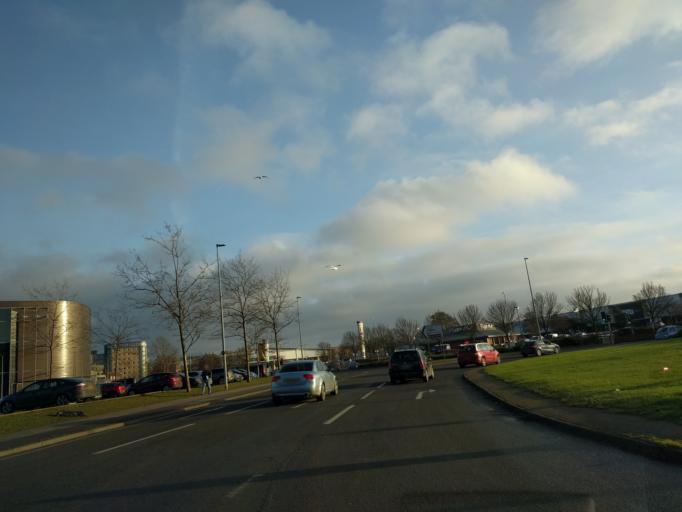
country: GB
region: England
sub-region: Lincolnshire
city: Lincoln
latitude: 53.2268
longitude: -0.5498
